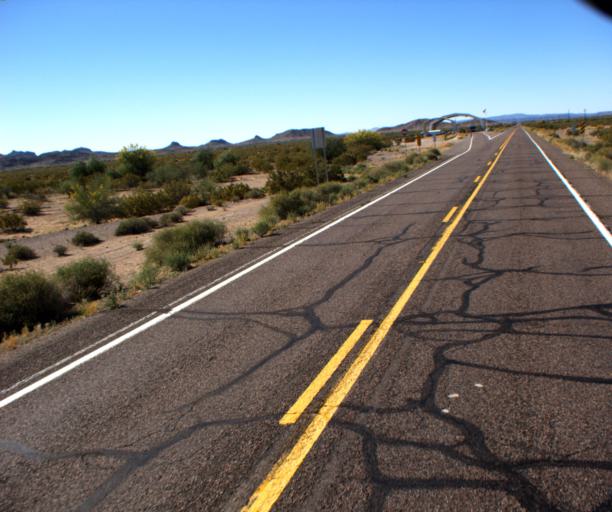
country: US
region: Arizona
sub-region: Maricopa County
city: Gila Bend
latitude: 32.7177
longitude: -112.8411
